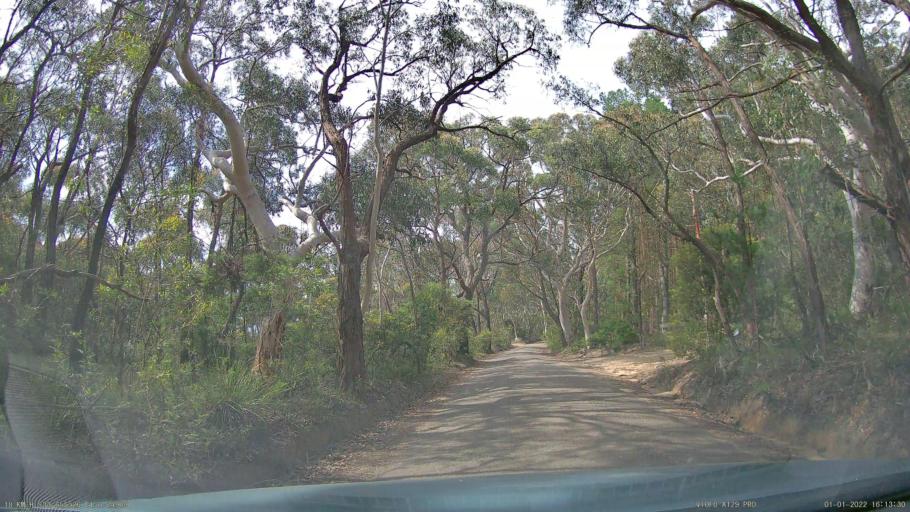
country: AU
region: New South Wales
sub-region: Blue Mountains Municipality
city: Blackheath
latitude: -33.6555
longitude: 150.2497
